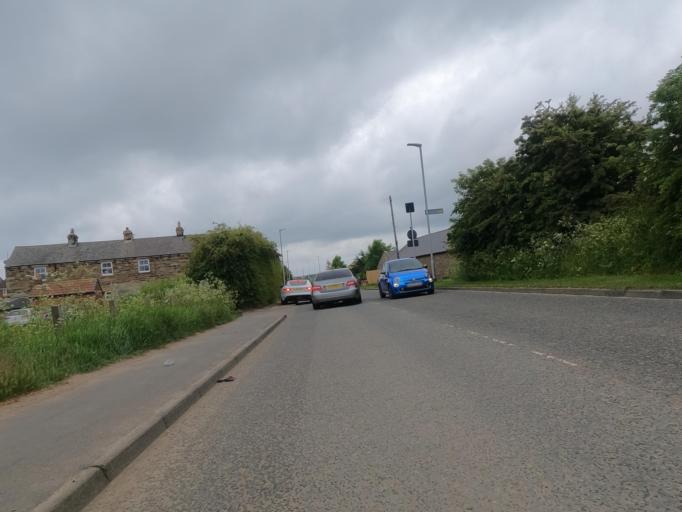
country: GB
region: England
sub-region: Northumberland
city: Blyth
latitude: 55.1055
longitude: -1.5283
